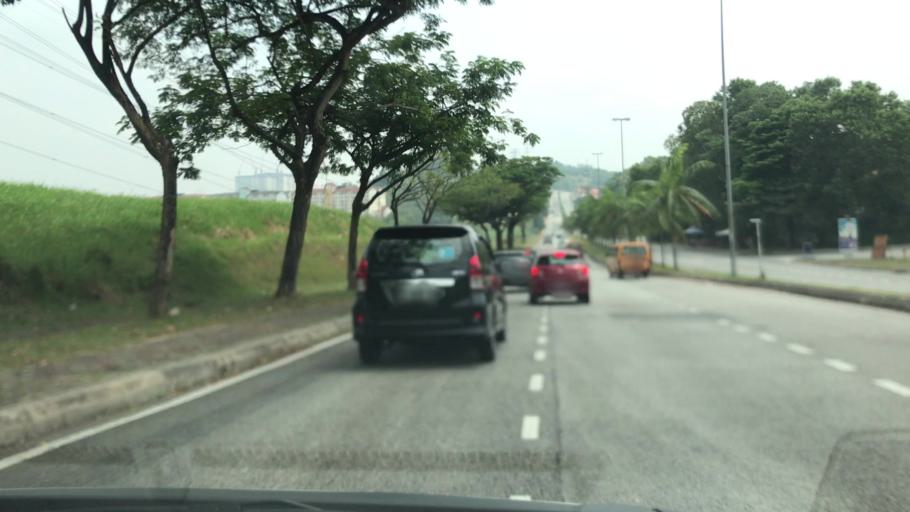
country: MY
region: Selangor
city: Kampong Baharu Balakong
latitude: 3.0306
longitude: 101.6801
